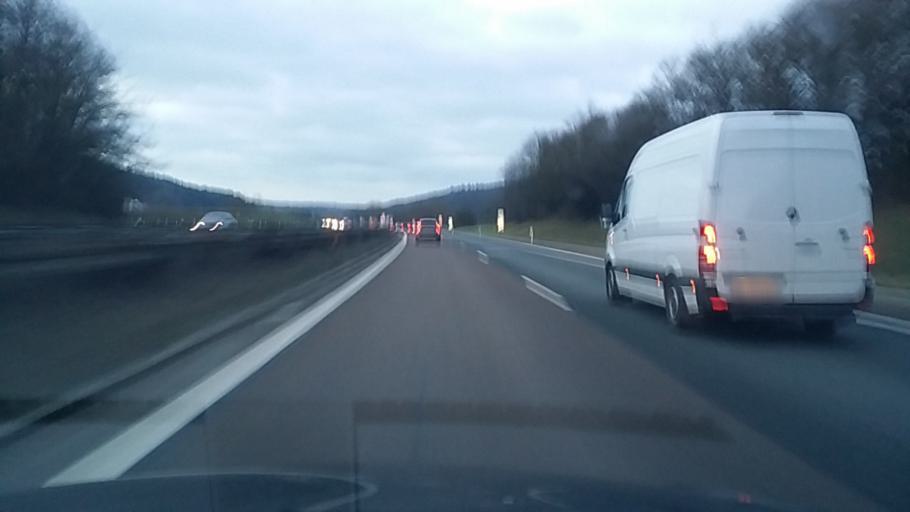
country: DE
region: Bavaria
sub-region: Regierungsbezirk Mittelfranken
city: Altdorf
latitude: 49.3604
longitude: 11.4286
